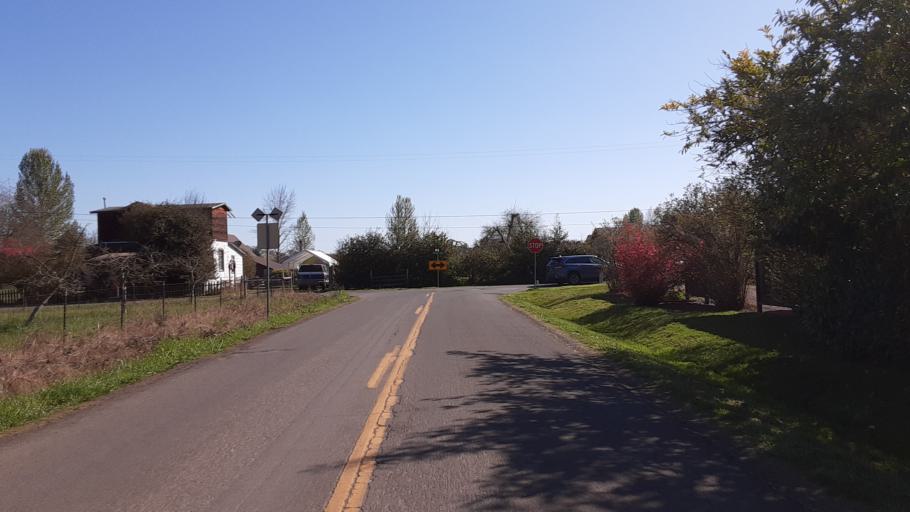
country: US
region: Oregon
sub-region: Benton County
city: Corvallis
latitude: 44.5391
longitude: -123.2556
